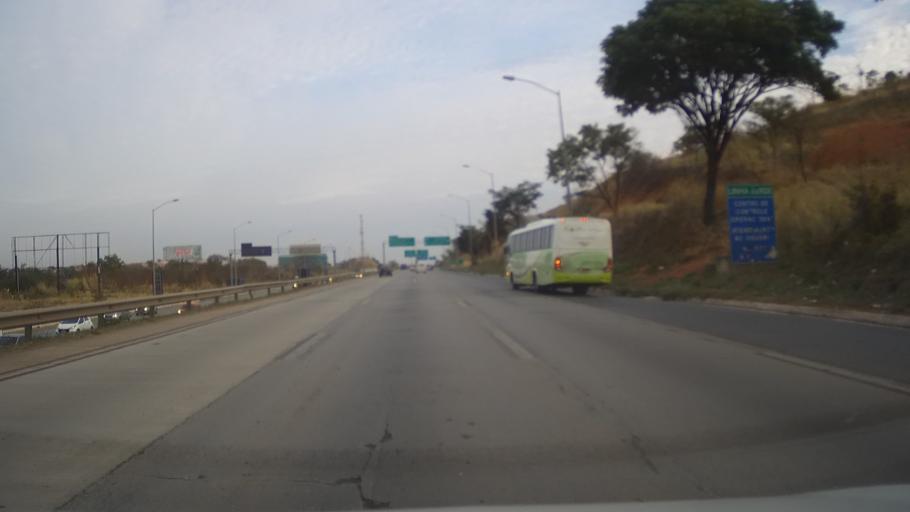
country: BR
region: Minas Gerais
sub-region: Vespasiano
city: Vespasiano
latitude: -19.7668
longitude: -43.9482
